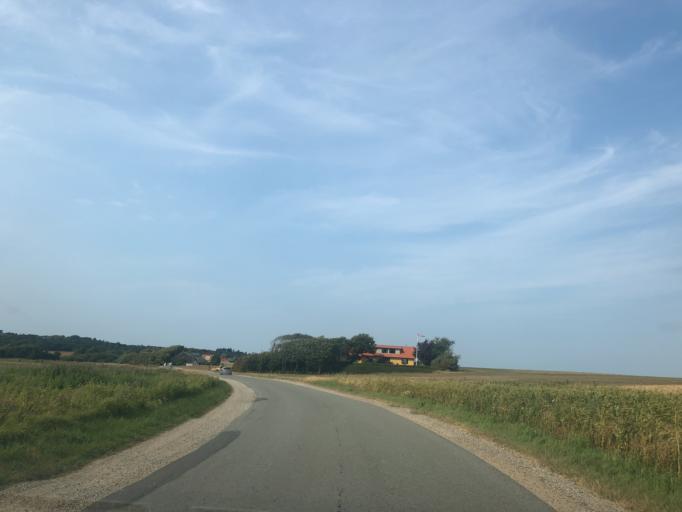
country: DK
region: North Denmark
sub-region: Morso Kommune
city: Nykobing Mors
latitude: 56.8249
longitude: 9.0382
